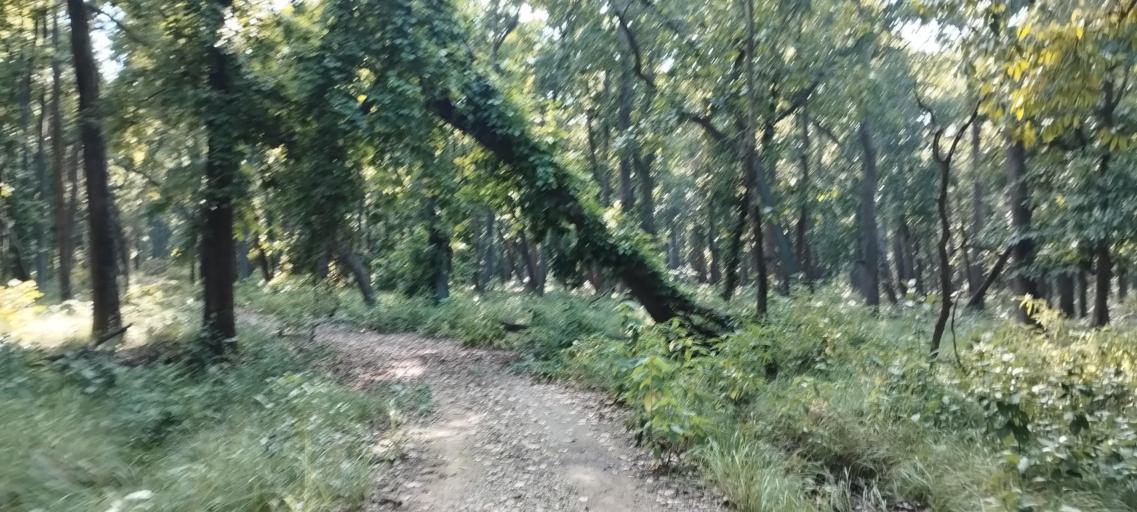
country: NP
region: Far Western
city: Tikapur
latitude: 28.5232
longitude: 81.2619
